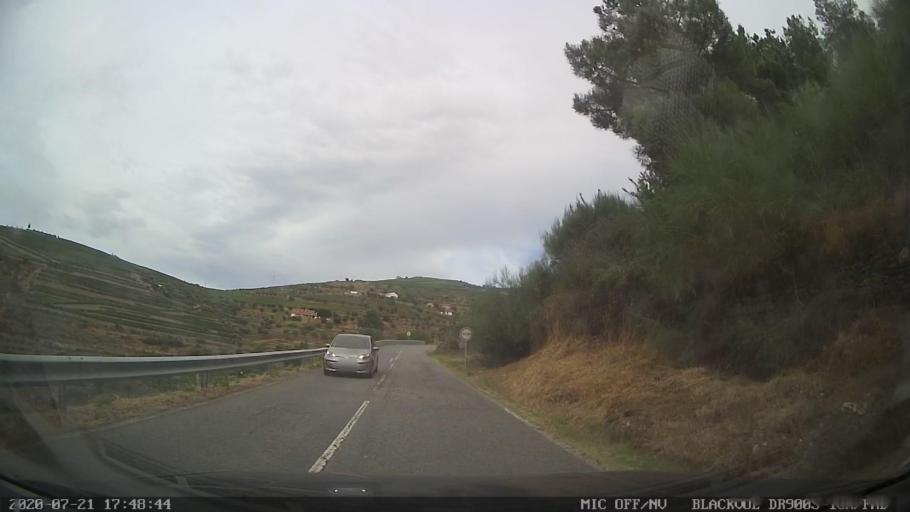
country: PT
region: Viseu
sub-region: Sao Joao da Pesqueira
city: Sao Joao da Pesqueira
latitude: 41.1741
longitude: -7.4828
